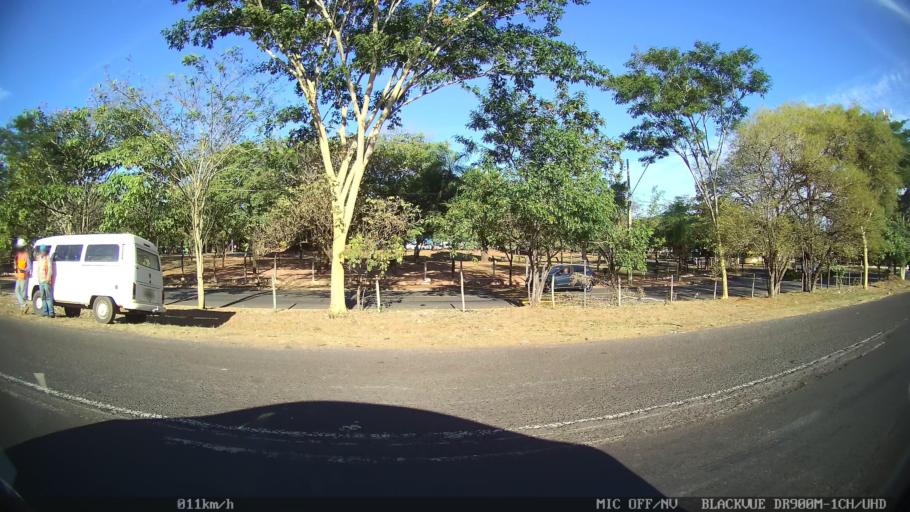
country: BR
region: Sao Paulo
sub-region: Sao Jose Do Rio Preto
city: Sao Jose do Rio Preto
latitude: -20.8341
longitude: -49.3629
